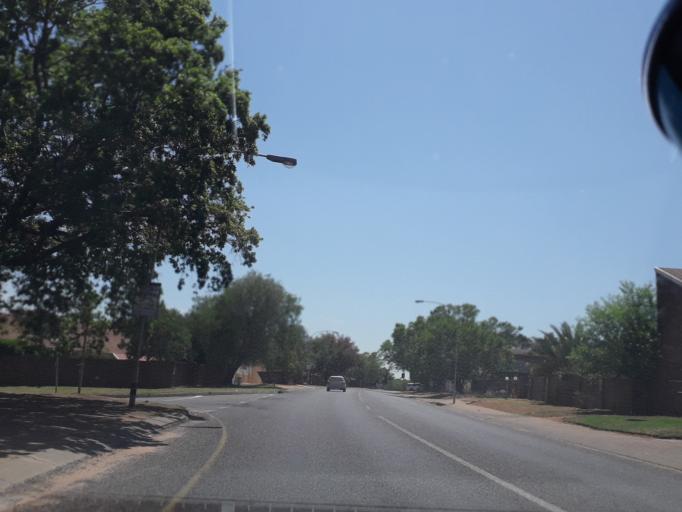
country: ZA
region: Gauteng
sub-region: City of Tshwane Metropolitan Municipality
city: Centurion
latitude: -25.8923
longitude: 28.1471
